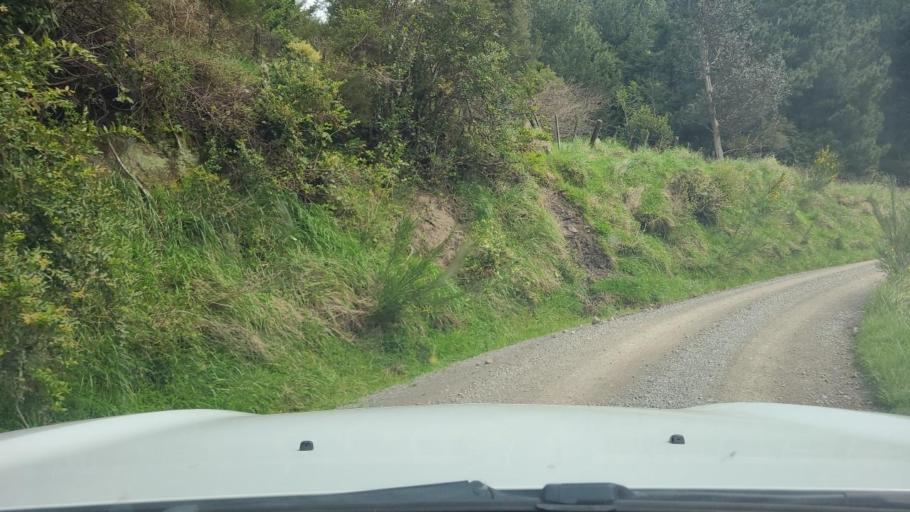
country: NZ
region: Wellington
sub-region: Masterton District
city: Masterton
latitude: -40.9333
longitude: 175.5022
